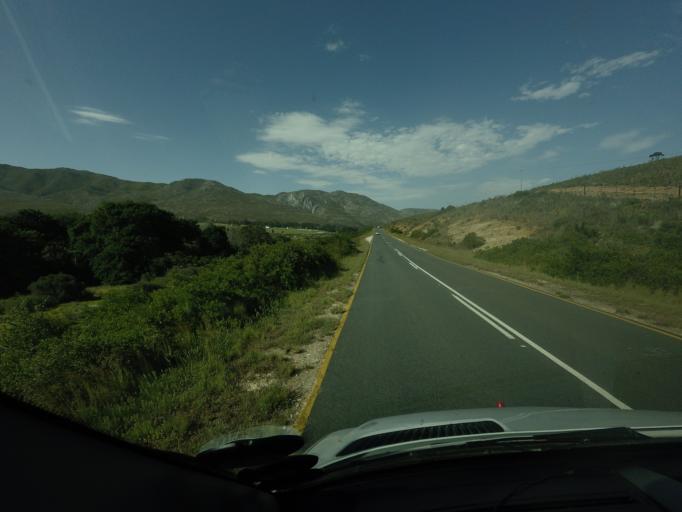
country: ZA
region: Western Cape
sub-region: Overberg District Municipality
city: Caledon
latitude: -34.4192
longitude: 19.5379
